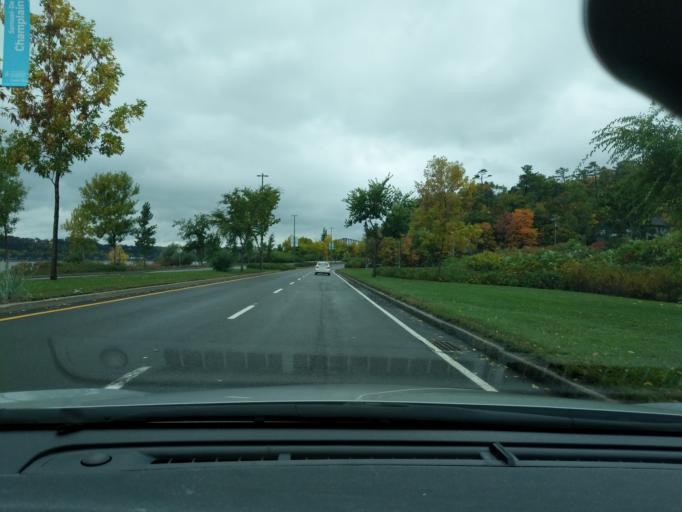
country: CA
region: Quebec
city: Quebec
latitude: 46.7608
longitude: -71.2659
